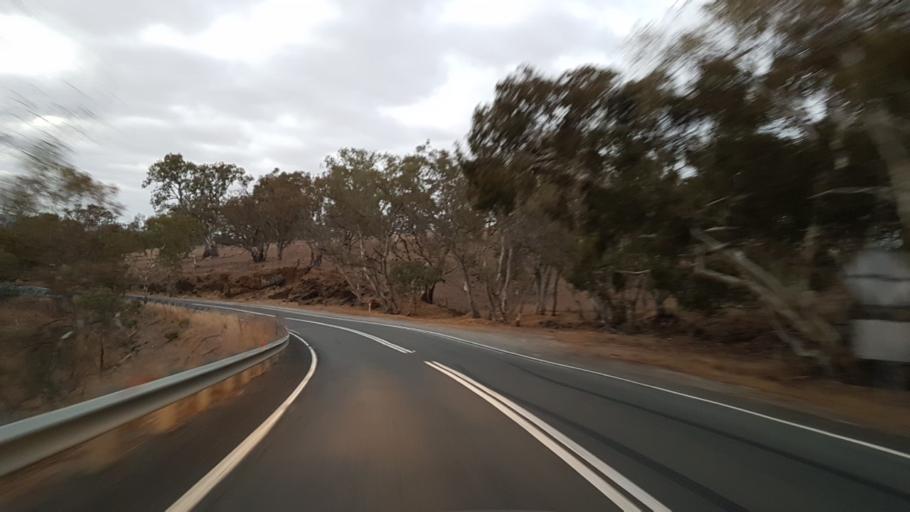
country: AU
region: South Australia
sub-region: Mount Barker
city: Nairne
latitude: -35.0313
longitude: 138.9638
